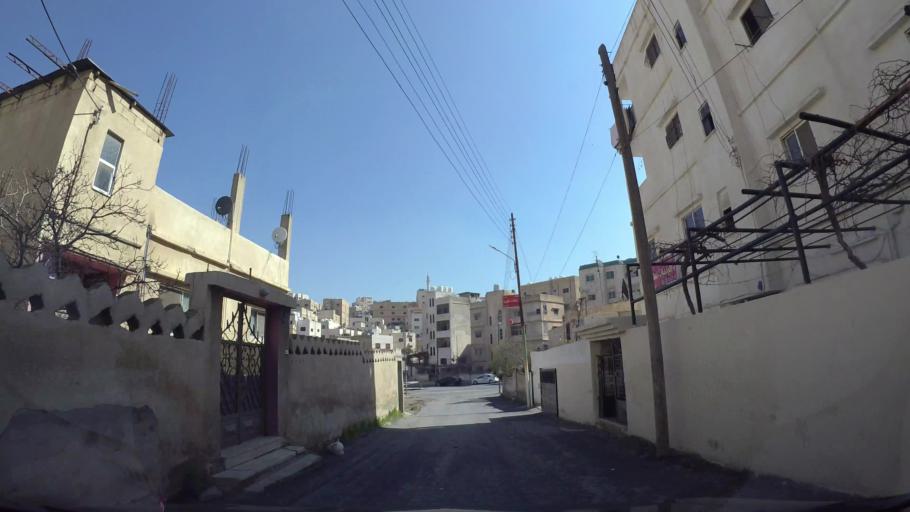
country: JO
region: Amman
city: Amman
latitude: 31.9859
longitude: 35.9830
